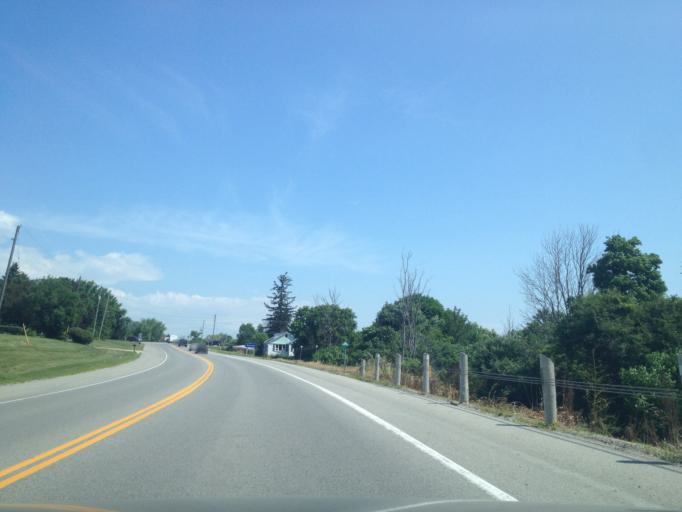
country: CA
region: Ontario
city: Huron East
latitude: 43.4586
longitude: -81.2058
